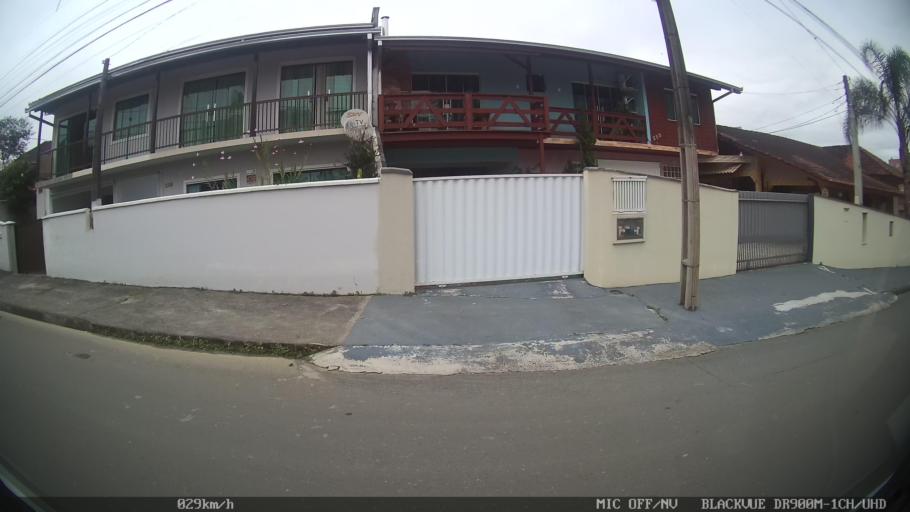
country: BR
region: Santa Catarina
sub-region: Joinville
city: Joinville
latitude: -26.2693
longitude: -48.8886
